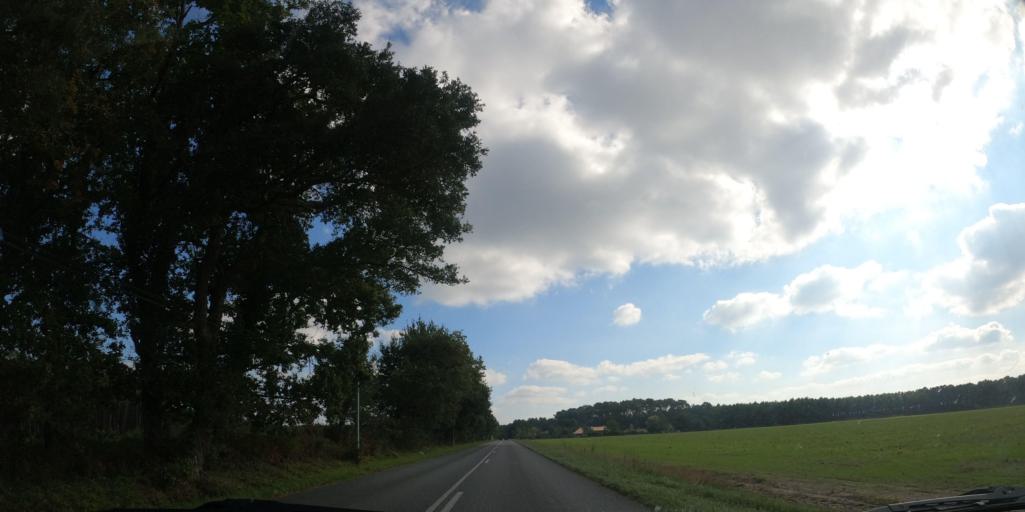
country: FR
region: Aquitaine
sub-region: Departement des Landes
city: Soustons
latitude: 43.7426
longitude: -1.2996
